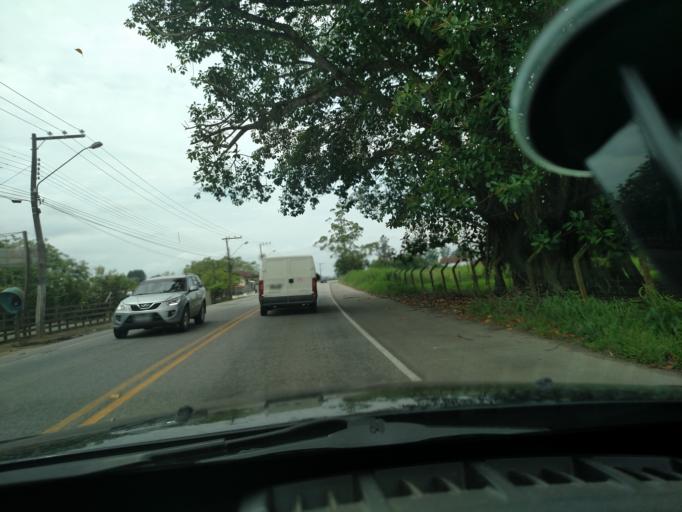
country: BR
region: Santa Catarina
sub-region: Itajai
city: Itajai
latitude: -26.8742
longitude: -48.7889
